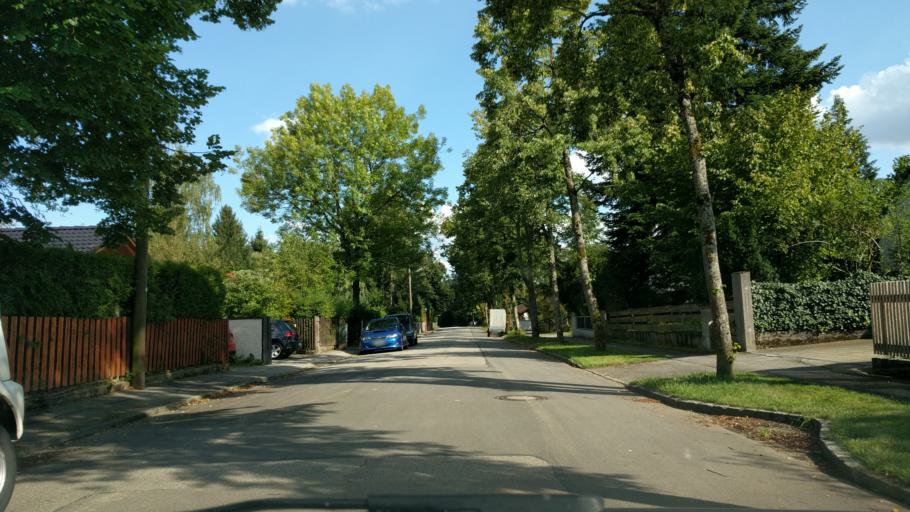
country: DE
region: Bavaria
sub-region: Upper Bavaria
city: Oberhaching
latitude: 48.0158
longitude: 11.5862
